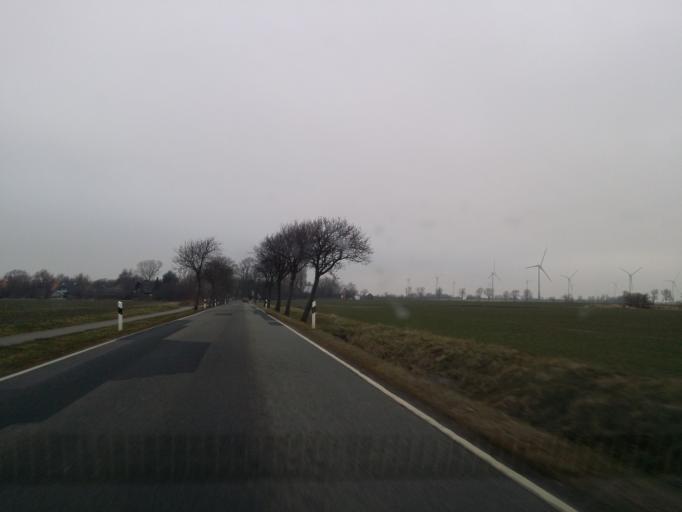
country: DE
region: Schleswig-Holstein
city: Grossenbrode
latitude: 54.4682
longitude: 11.1006
